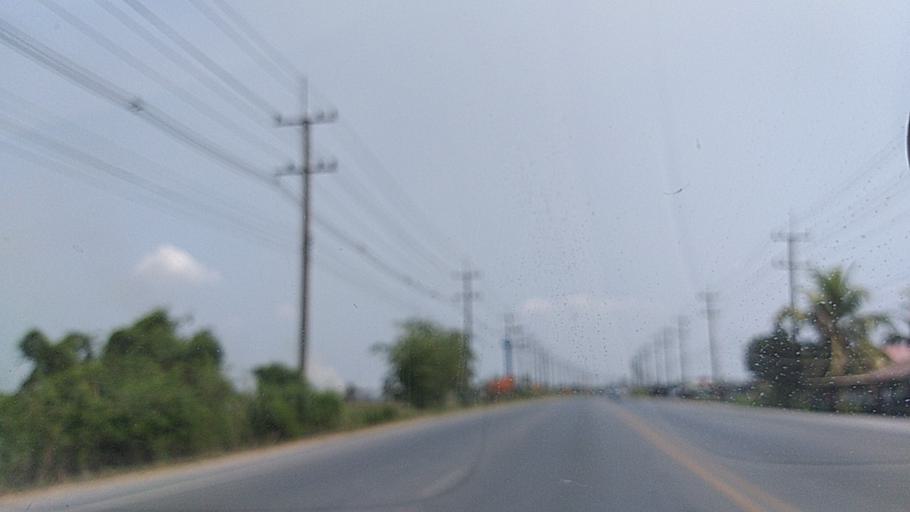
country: TH
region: Bangkok
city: Nong Chok
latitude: 13.9662
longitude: 100.9292
